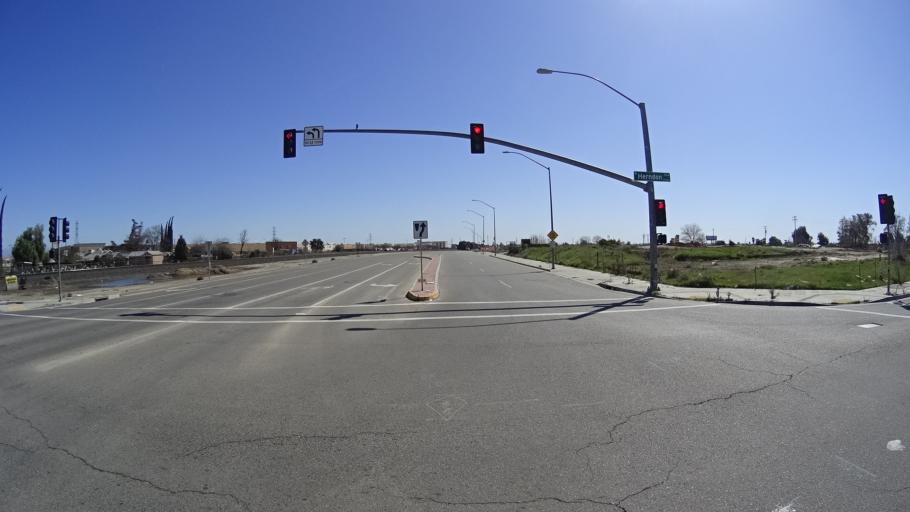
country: US
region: California
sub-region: Fresno County
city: Biola
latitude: 36.8338
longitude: -119.9147
